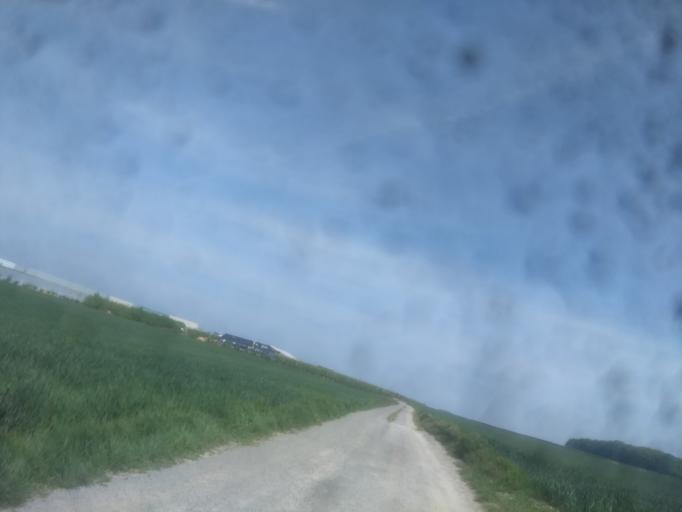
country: FR
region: Nord-Pas-de-Calais
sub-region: Departement du Pas-de-Calais
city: Beaurains
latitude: 50.2598
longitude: 2.8080
